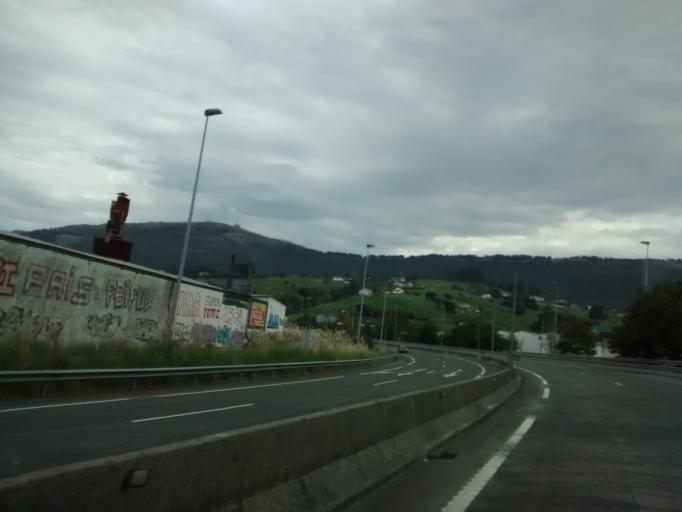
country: ES
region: Cantabria
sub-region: Provincia de Cantabria
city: El Astillero
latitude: 43.3961
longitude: -3.8141
